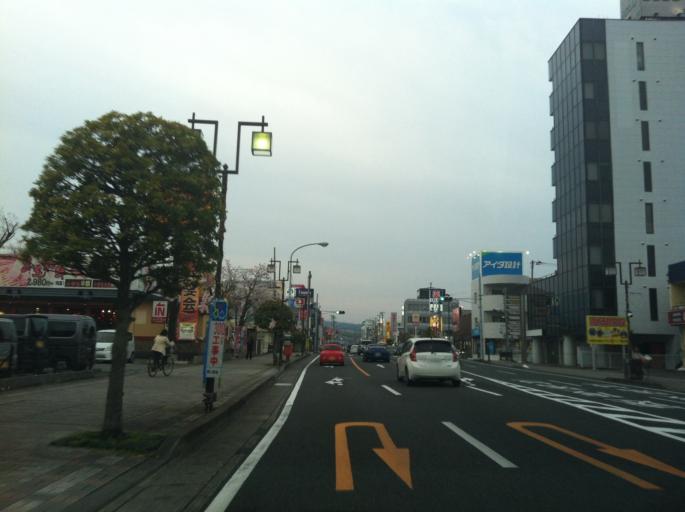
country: JP
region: Shizuoka
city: Numazu
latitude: 35.1105
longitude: 138.8590
